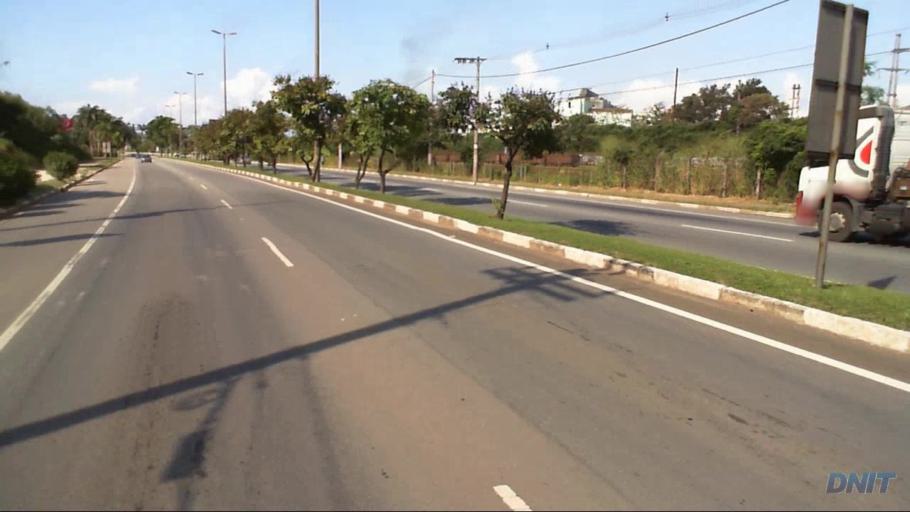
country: BR
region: Minas Gerais
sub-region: Ipatinga
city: Ipatinga
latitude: -19.4830
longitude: -42.5492
